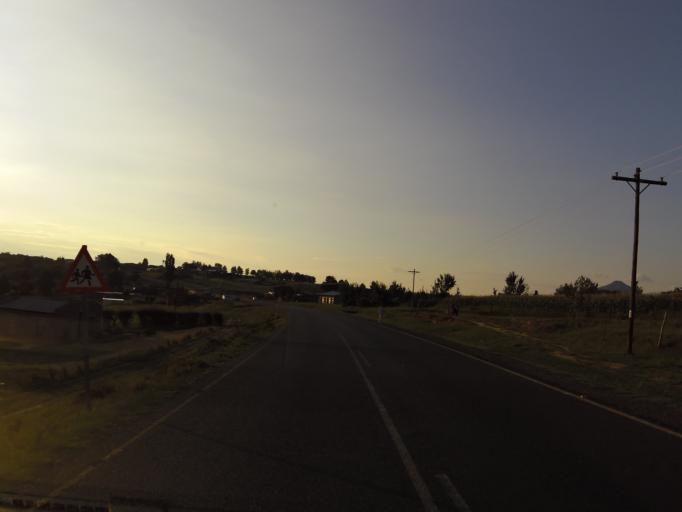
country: LS
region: Leribe
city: Leribe
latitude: -28.9369
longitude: 28.1660
